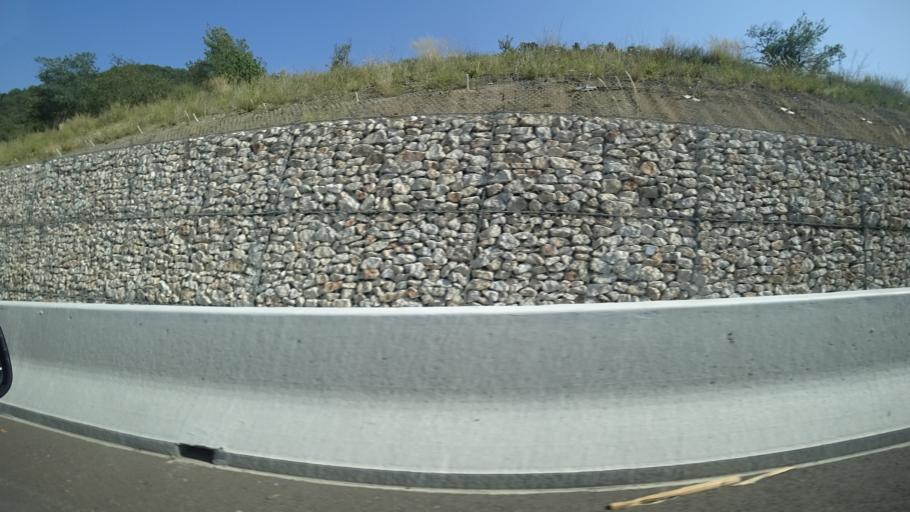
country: FR
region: Languedoc-Roussillon
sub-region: Departement des Pyrenees-Orientales
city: Vernet-les-Bains
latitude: 42.5612
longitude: 2.3023
